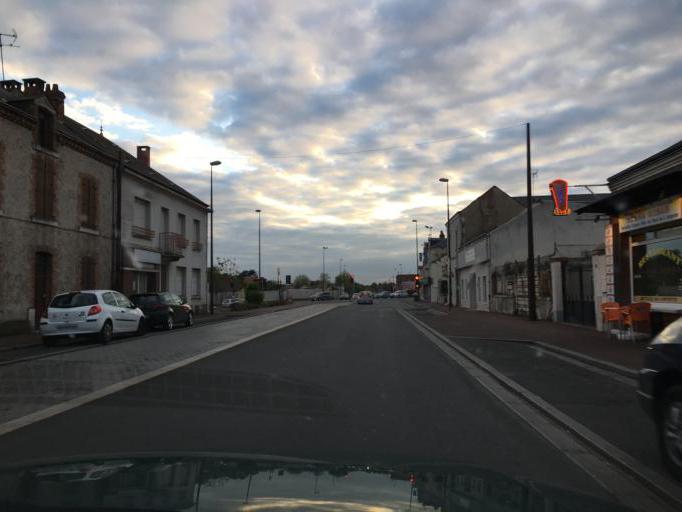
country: FR
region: Centre
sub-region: Departement du Loiret
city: Saint-Jean-de-la-Ruelle
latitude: 47.8989
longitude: 1.8752
